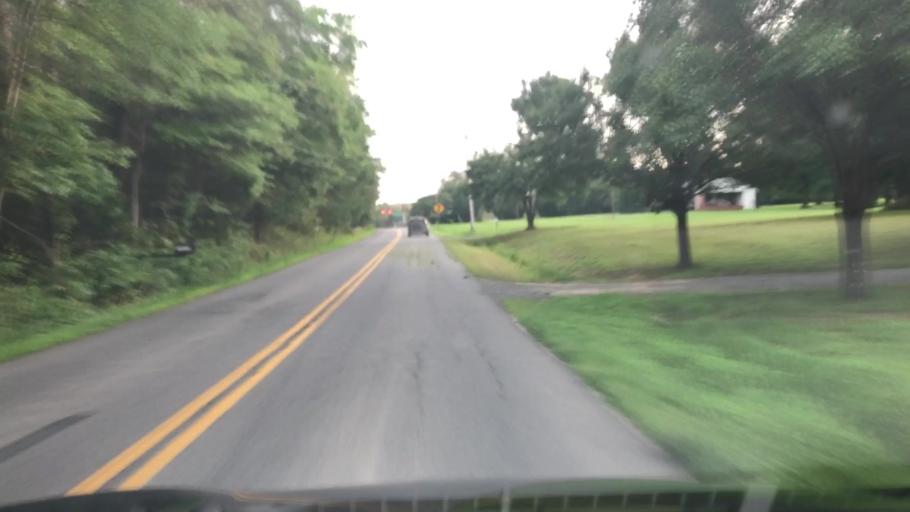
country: US
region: Virginia
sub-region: Fauquier County
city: Bealeton
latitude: 38.5019
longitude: -77.6903
